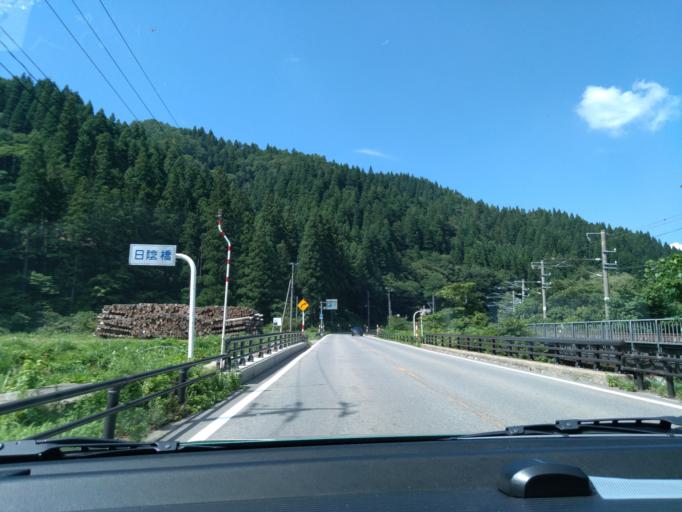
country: JP
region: Akita
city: Kakunodatemachi
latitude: 39.6409
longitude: 140.6607
